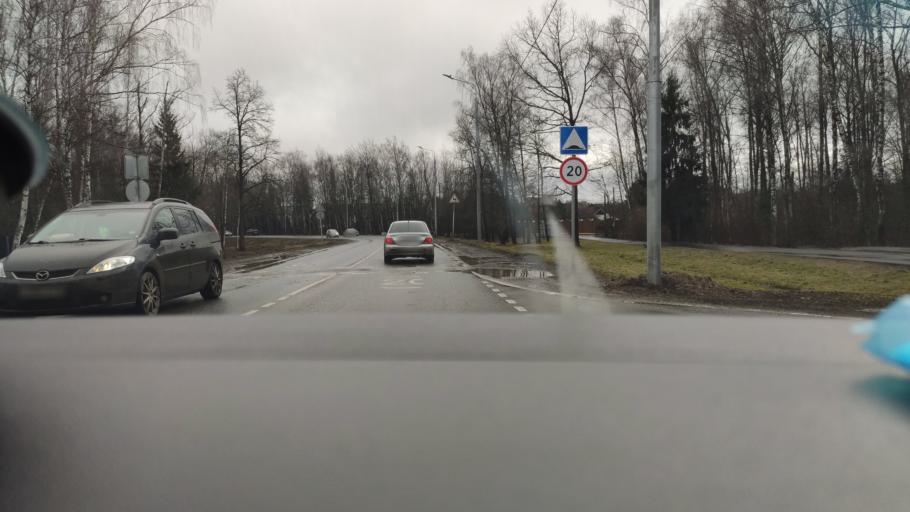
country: RU
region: Moskovskaya
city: Troitsk
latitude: 55.3058
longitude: 37.1870
